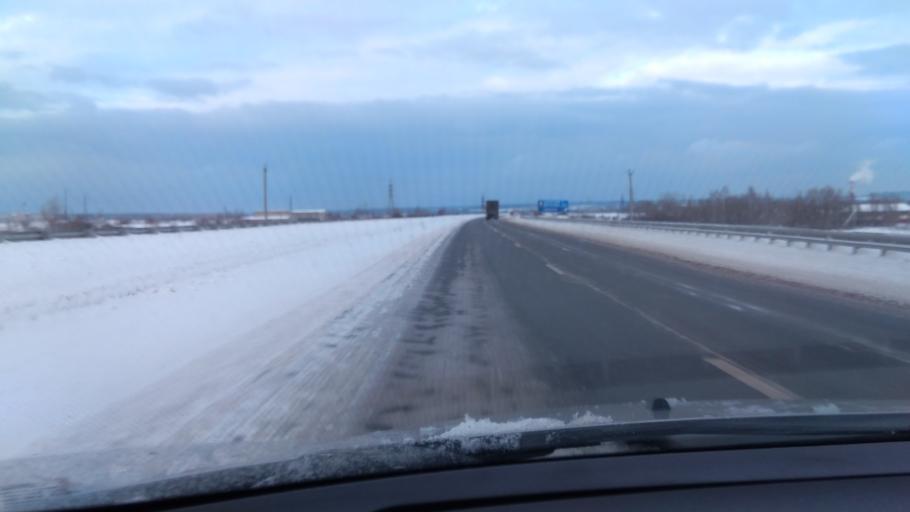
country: RU
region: Sverdlovsk
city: Tsementnyy
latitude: 57.4734
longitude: 60.1812
